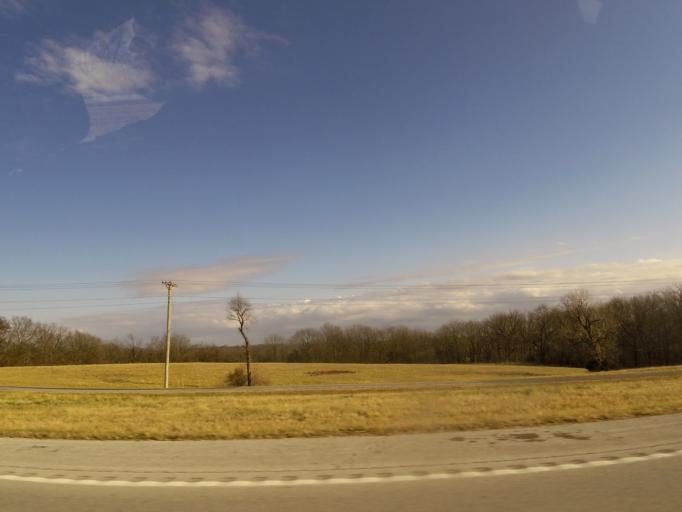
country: US
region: Missouri
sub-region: Ralls County
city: New London
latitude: 39.6468
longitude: -91.4193
